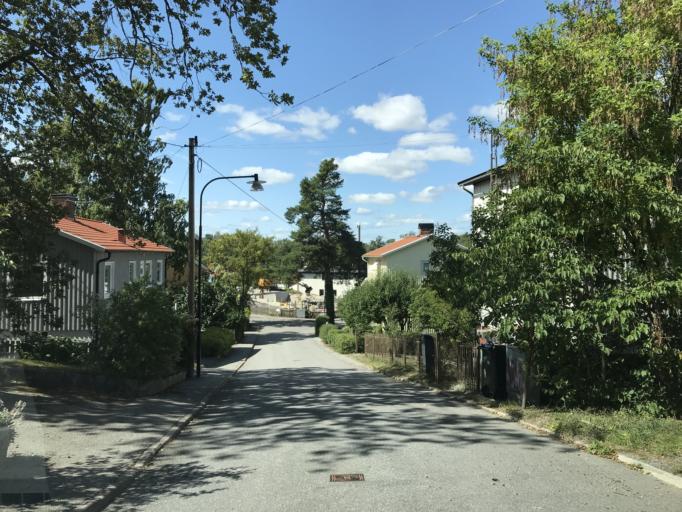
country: SE
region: Stockholm
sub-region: Huddinge Kommun
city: Segeltorp
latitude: 59.2994
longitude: 17.9531
